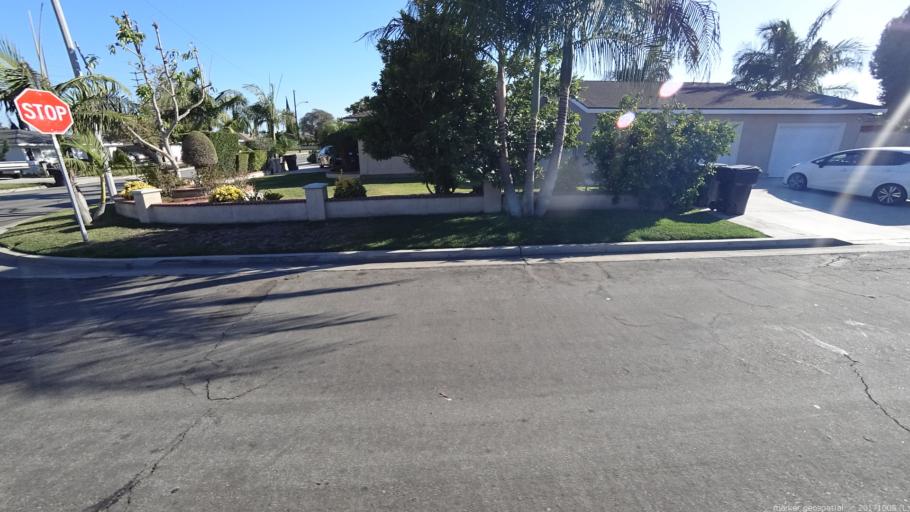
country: US
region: California
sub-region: Orange County
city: Stanton
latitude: 33.7917
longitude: -117.9805
